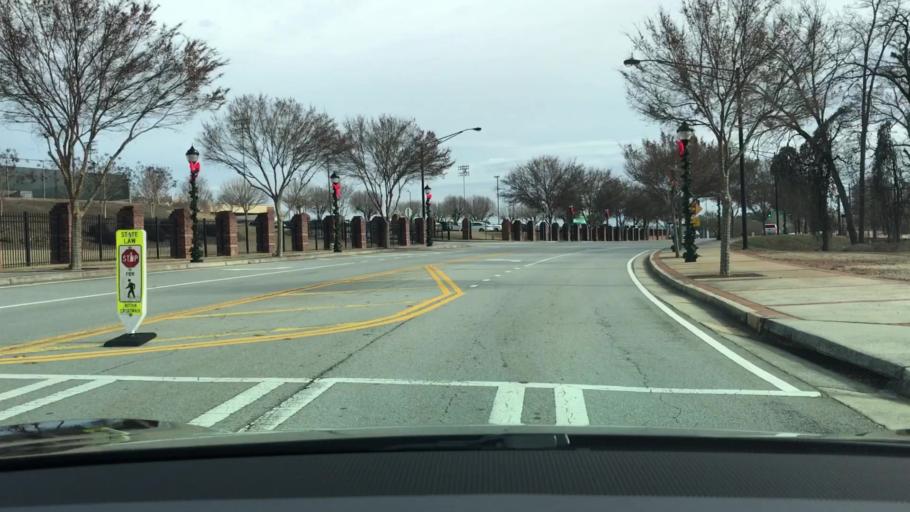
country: US
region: Georgia
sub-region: Gwinnett County
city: Buford
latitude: 34.1327
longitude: -83.9892
